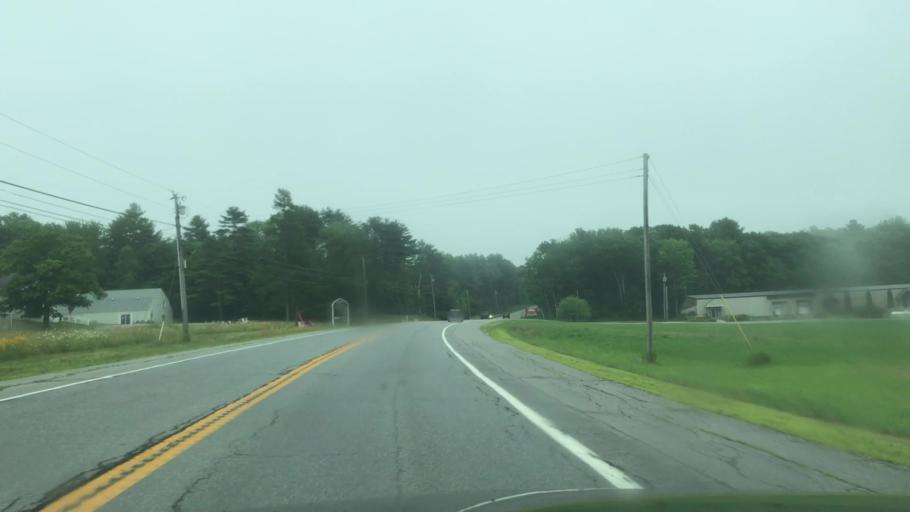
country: US
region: Maine
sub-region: Lincoln County
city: Waldoboro
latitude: 44.1034
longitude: -69.4286
